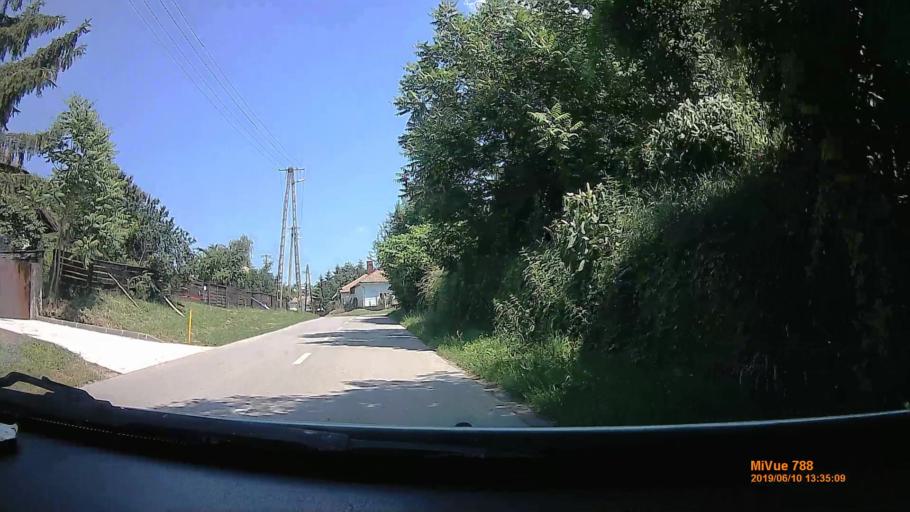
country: HU
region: Szabolcs-Szatmar-Bereg
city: Tiszadob
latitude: 48.0105
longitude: 21.1622
